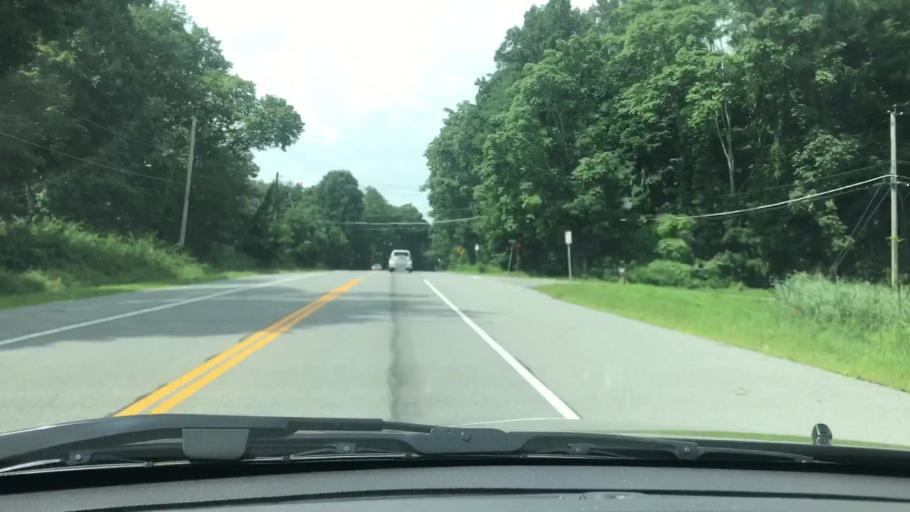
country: US
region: New York
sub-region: Westchester County
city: Mount Kisco
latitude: 41.1965
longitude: -73.6914
